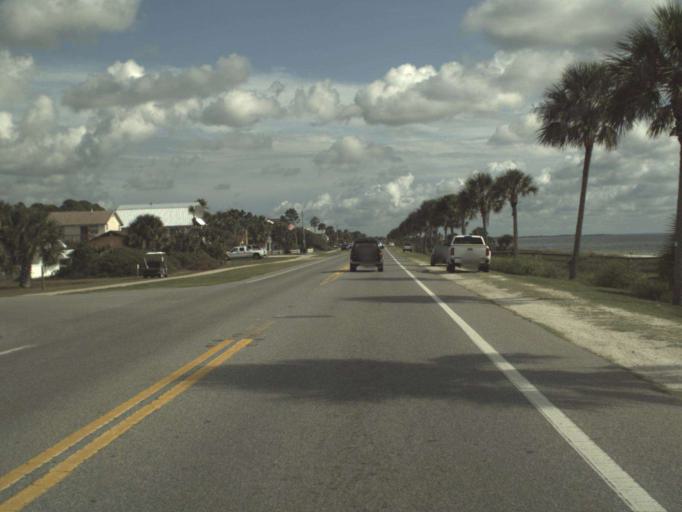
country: US
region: Florida
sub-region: Bay County
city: Mexico Beach
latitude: 29.9358
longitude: -85.4009
